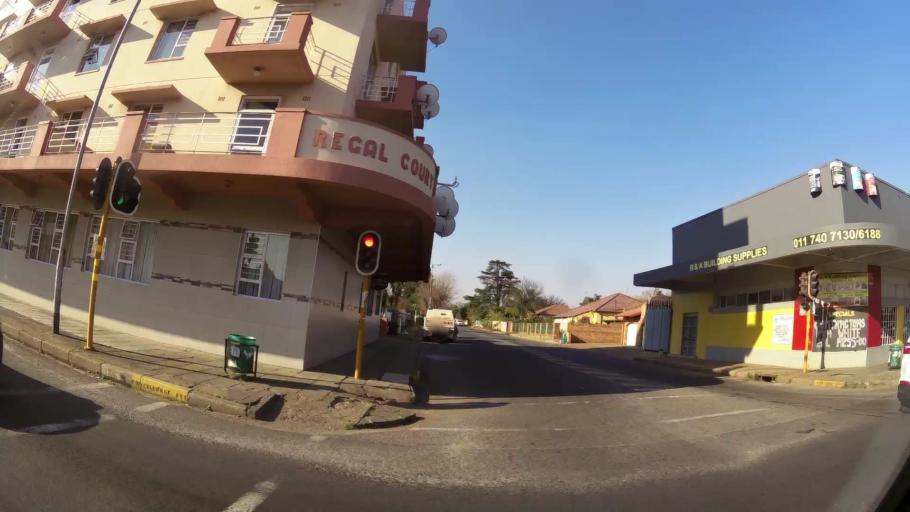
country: ZA
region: Gauteng
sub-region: Ekurhuleni Metropolitan Municipality
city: Brakpan
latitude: -26.2432
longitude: 28.3679
